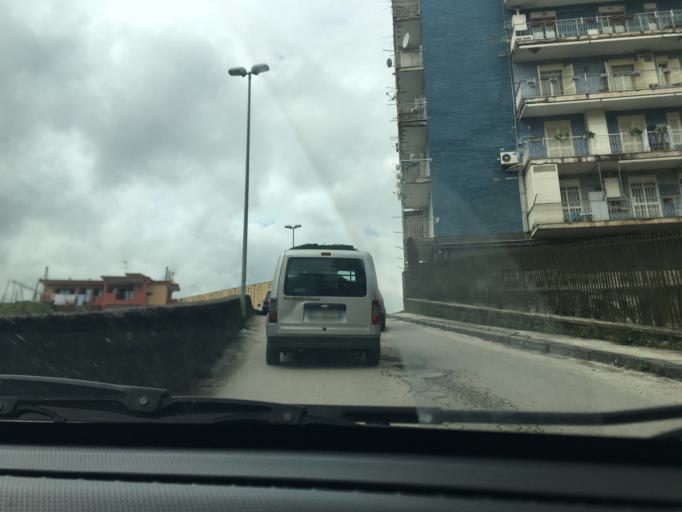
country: IT
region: Campania
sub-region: Provincia di Napoli
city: Mugnano di Napoli
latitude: 40.8947
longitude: 14.2020
